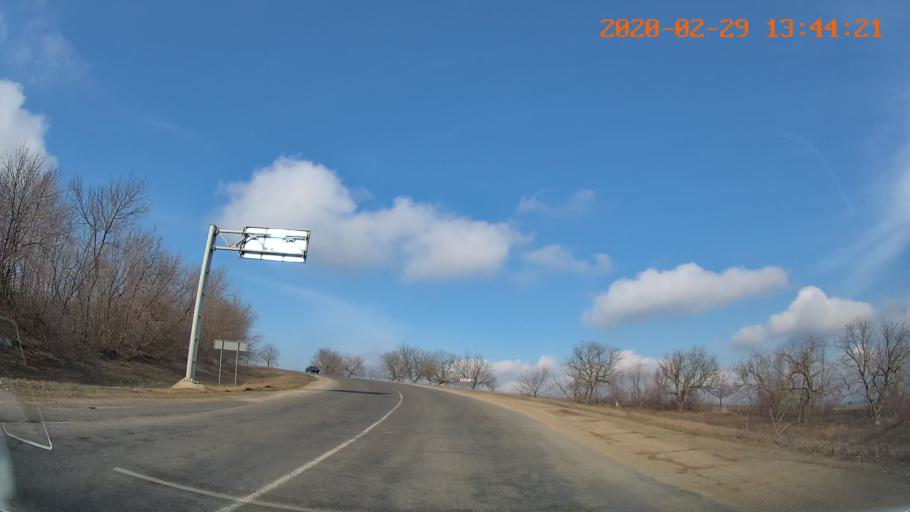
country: MD
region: Floresti
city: Leninskiy
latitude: 47.8395
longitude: 28.5240
